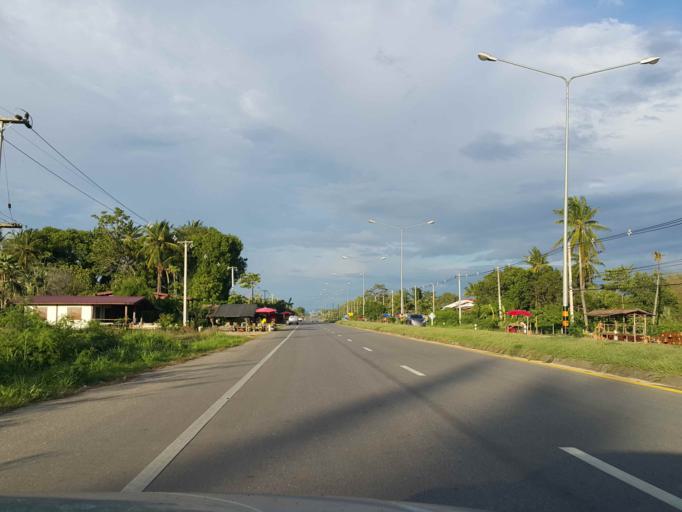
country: TH
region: Sukhothai
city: Ban Dan Lan Hoi
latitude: 16.9228
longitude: 99.3976
